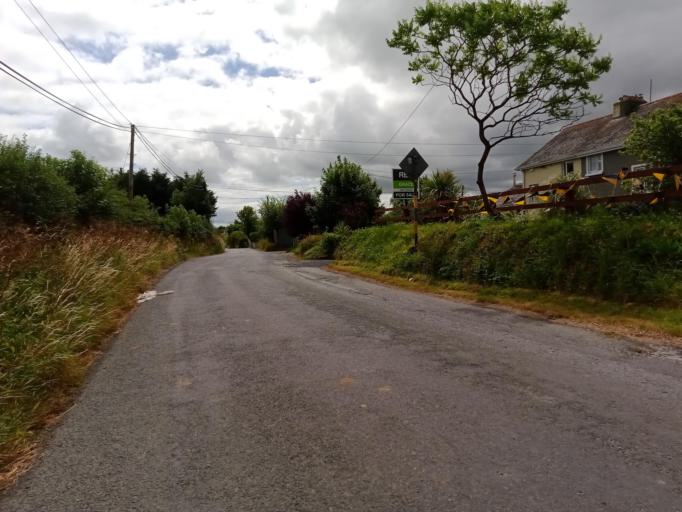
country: IE
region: Leinster
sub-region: Kilkenny
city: Callan
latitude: 52.5583
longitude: -7.3799
